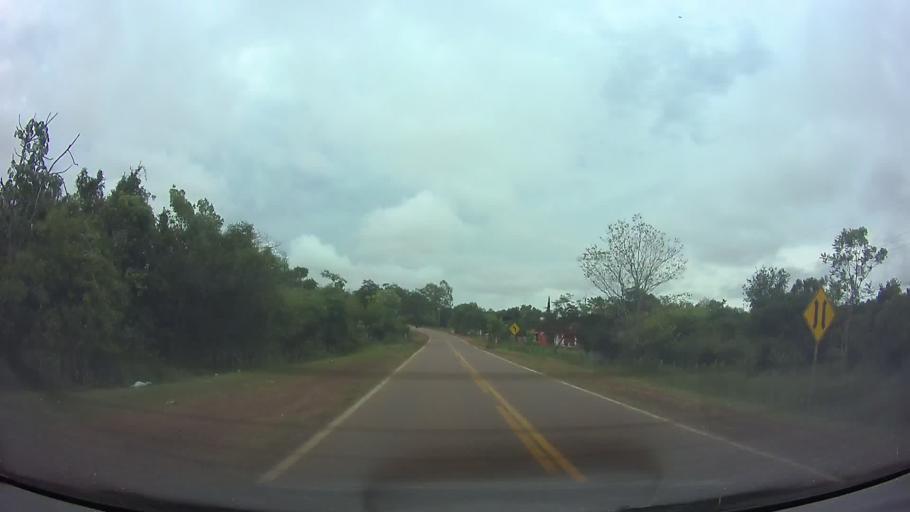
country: PY
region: Paraguari
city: Carapegua
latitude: -25.8002
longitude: -57.1923
